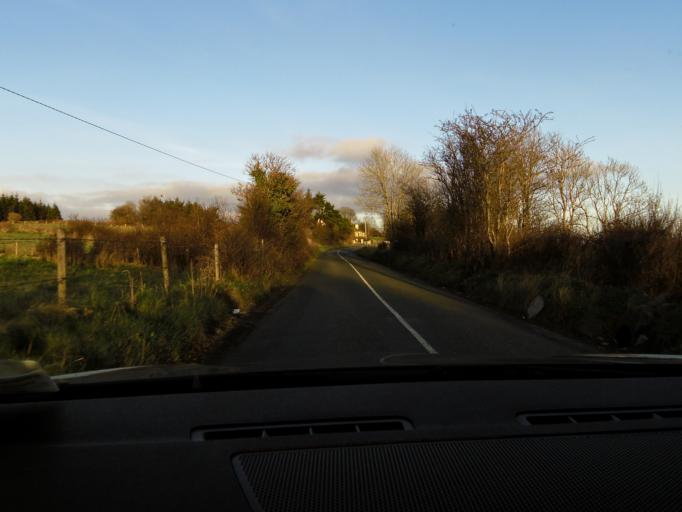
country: IE
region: Connaught
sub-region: Sligo
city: Tobercurry
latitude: 54.0504
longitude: -8.7005
